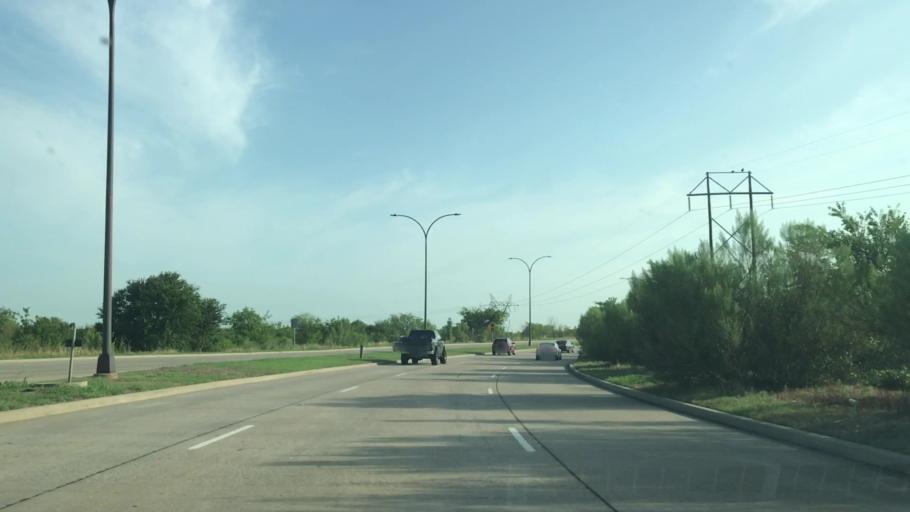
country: US
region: Texas
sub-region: Tarrant County
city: Arlington
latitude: 32.7767
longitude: -97.1363
